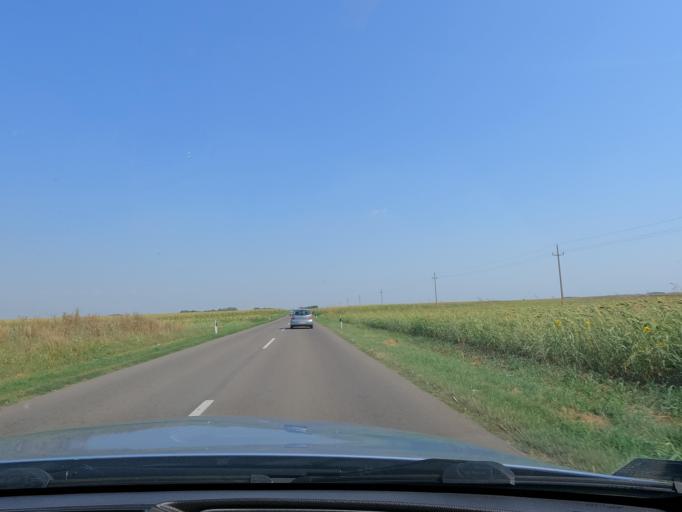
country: RS
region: Autonomna Pokrajina Vojvodina
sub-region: Severnobacki Okrug
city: Backa Topola
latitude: 45.7980
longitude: 19.6660
